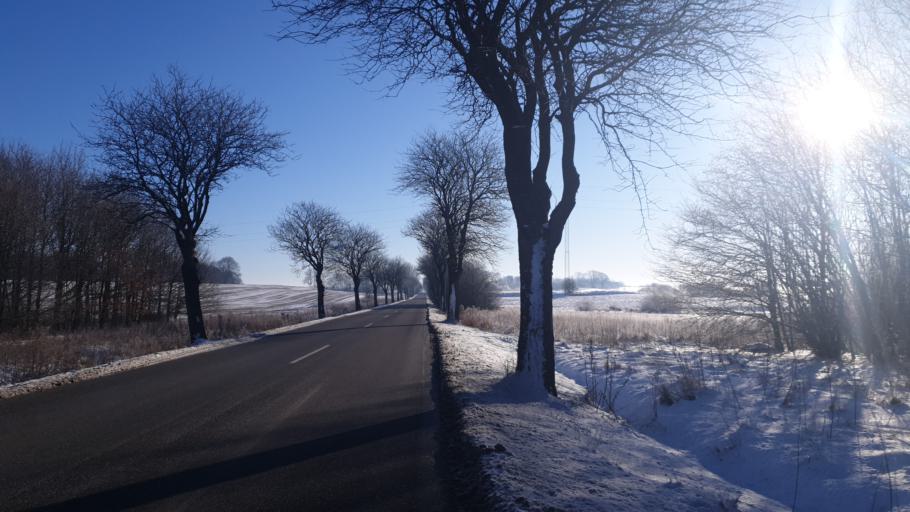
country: DK
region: Central Jutland
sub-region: Hedensted Kommune
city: Hedensted
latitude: 55.8003
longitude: 9.7252
